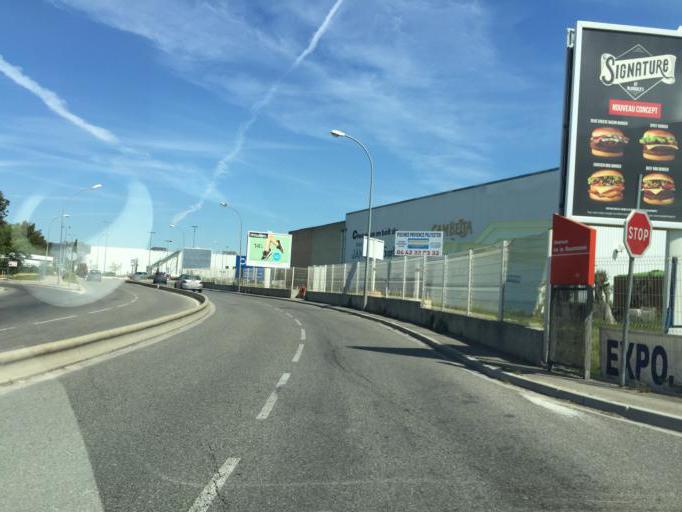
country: FR
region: Provence-Alpes-Cote d'Azur
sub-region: Departement des Bouches-du-Rhone
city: Aubagne
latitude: 43.2920
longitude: 5.5940
